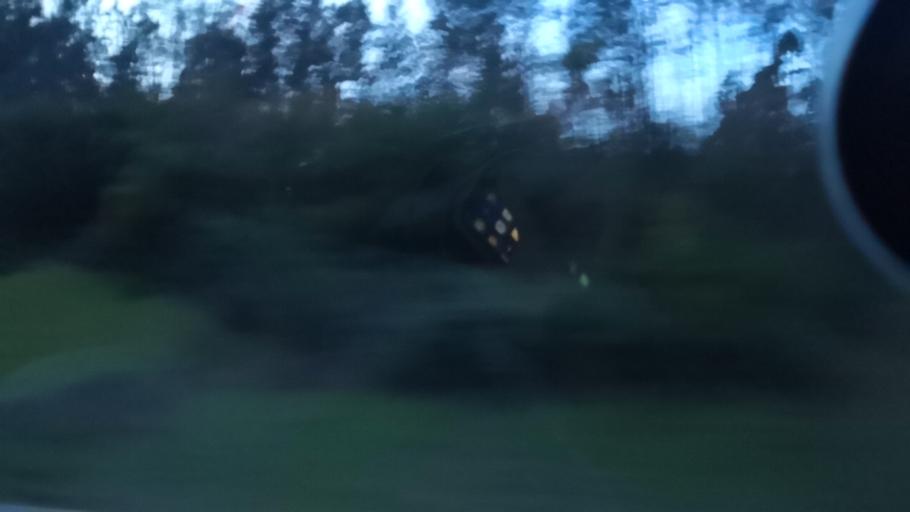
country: PT
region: Coimbra
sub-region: Soure
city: Soure
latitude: 40.0041
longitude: -8.6073
